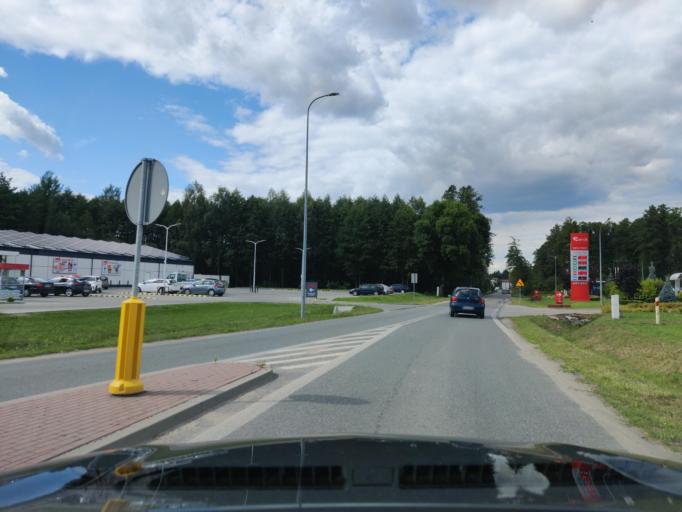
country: PL
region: Masovian Voivodeship
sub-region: Powiat sokolowski
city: Kosow Lacki
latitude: 52.5836
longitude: 22.1539
